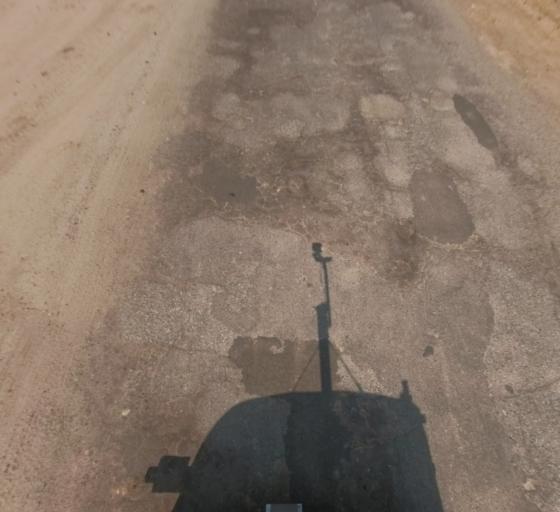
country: US
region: California
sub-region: Madera County
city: Fairmead
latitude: 37.1413
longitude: -120.1320
